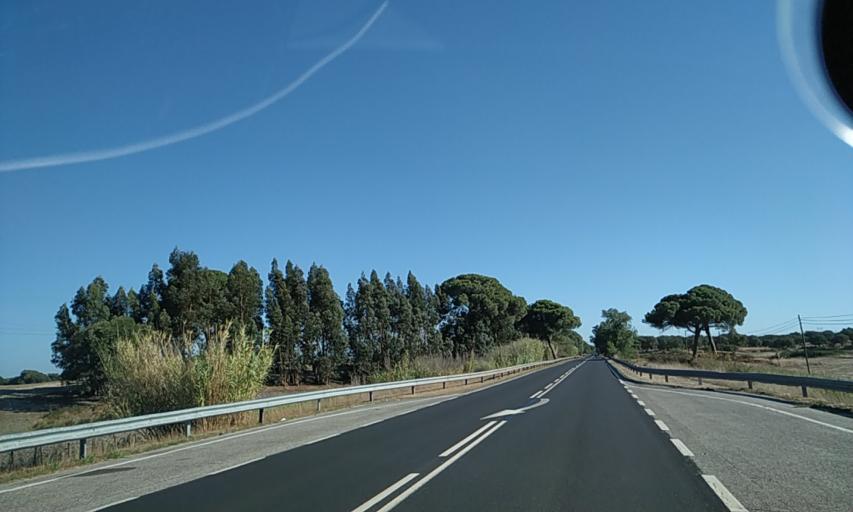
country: PT
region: Santarem
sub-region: Benavente
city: Samora Correia
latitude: 38.8639
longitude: -8.8812
